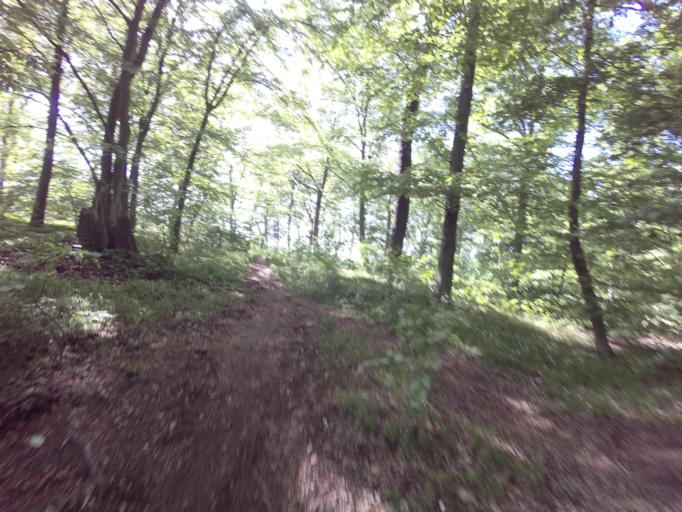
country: DE
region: Lower Saxony
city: Cremlingen
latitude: 52.2926
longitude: 10.6299
